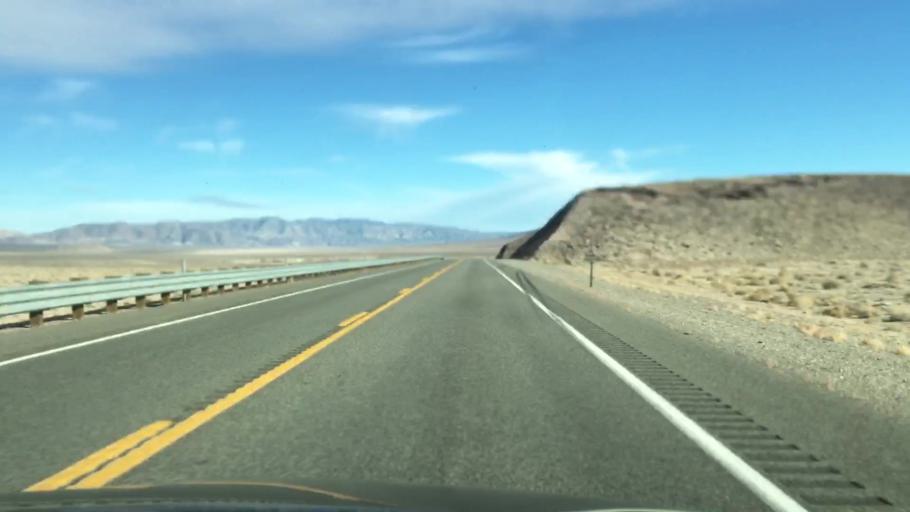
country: US
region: Nevada
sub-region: Mineral County
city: Hawthorne
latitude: 38.5455
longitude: -118.4106
